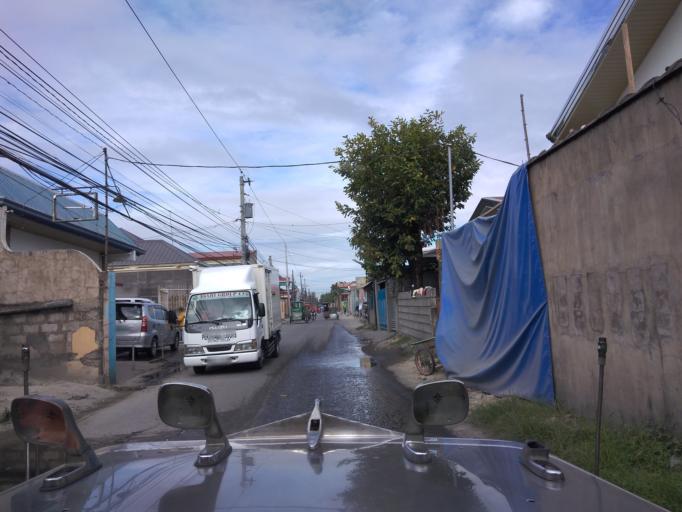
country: PH
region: Central Luzon
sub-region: Province of Pampanga
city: Mexico
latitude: 15.0670
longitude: 120.7176
